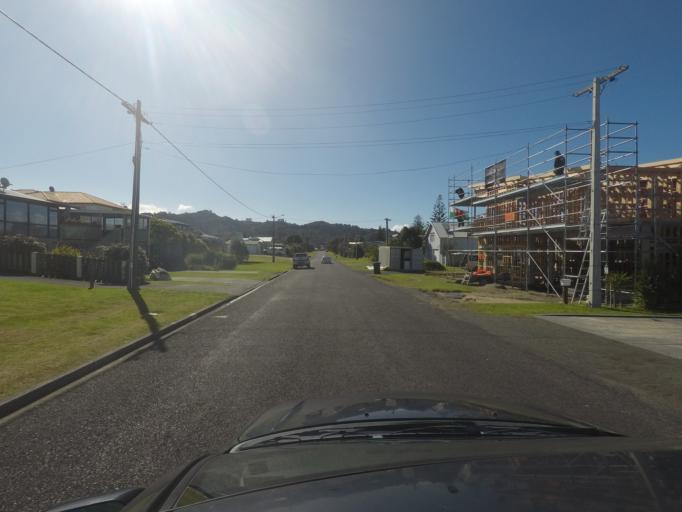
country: NZ
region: Bay of Plenty
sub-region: Western Bay of Plenty District
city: Waihi Beach
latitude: -37.4085
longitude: 175.9447
